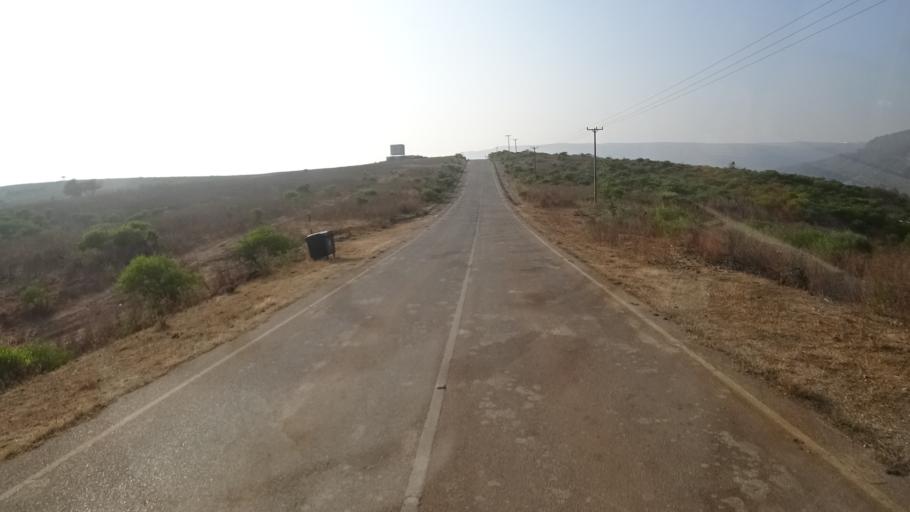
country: YE
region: Al Mahrah
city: Hawf
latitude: 16.7453
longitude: 53.3488
